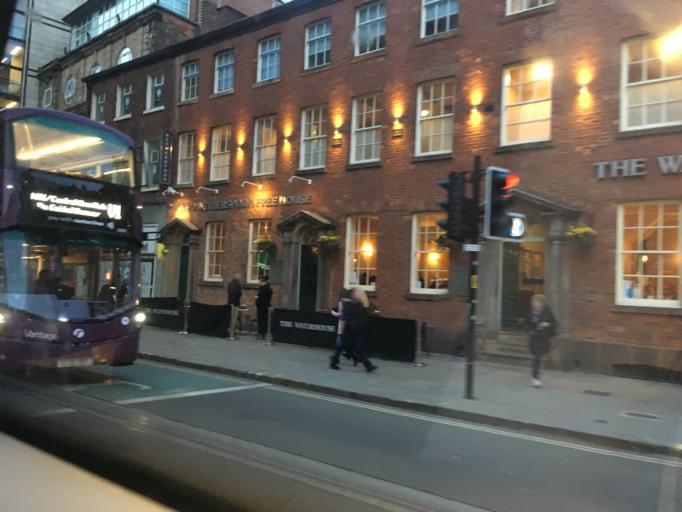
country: GB
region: England
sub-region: Manchester
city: Manchester
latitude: 53.4788
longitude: -2.2430
